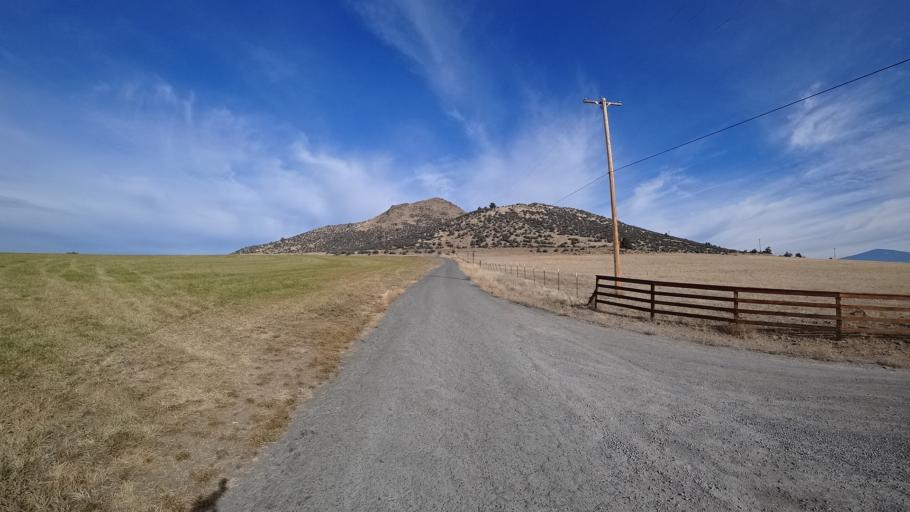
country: US
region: California
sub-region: Siskiyou County
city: Montague
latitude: 41.7057
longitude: -122.5154
